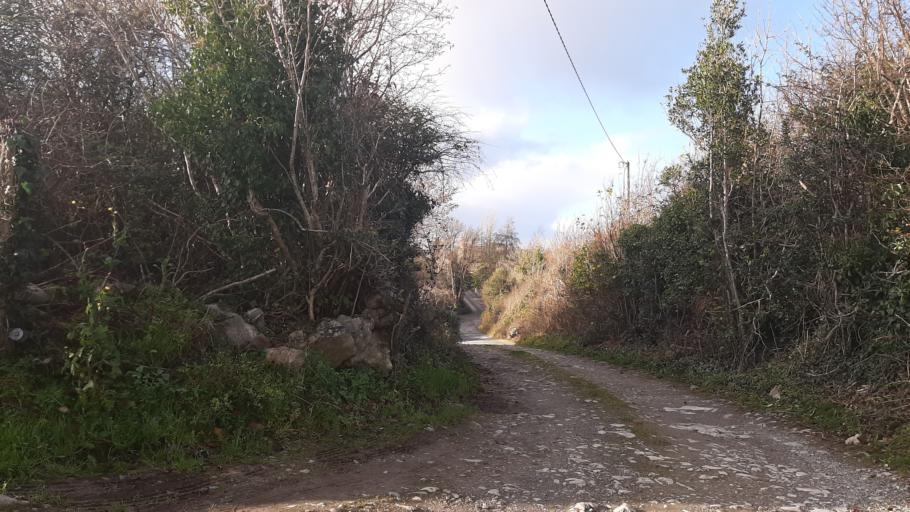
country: IE
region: Connaught
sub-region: County Galway
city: Gaillimh
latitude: 53.3021
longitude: -9.0611
